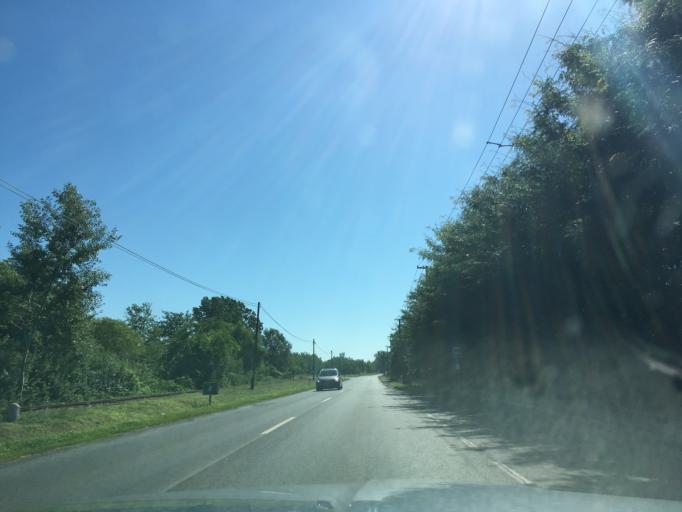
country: HU
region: Hajdu-Bihar
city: Debrecen
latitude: 47.5317
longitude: 21.6915
